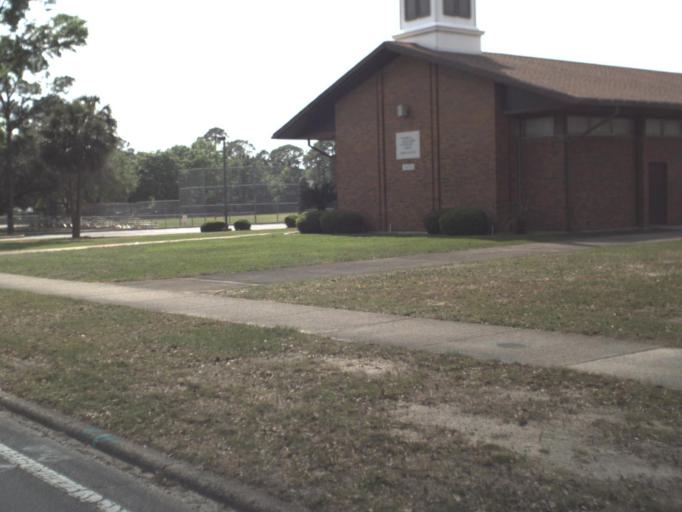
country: US
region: Florida
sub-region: Escambia County
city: Ferry Pass
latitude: 30.4833
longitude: -87.2030
